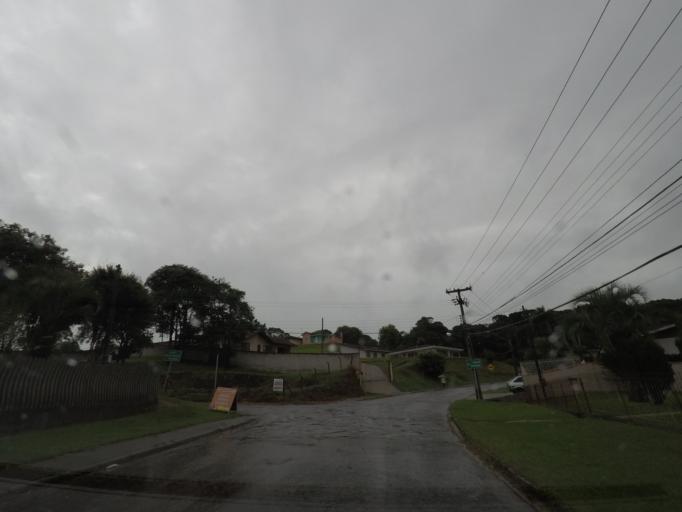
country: BR
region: Parana
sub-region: Campo Largo
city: Campo Largo
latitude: -25.4622
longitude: -49.4053
